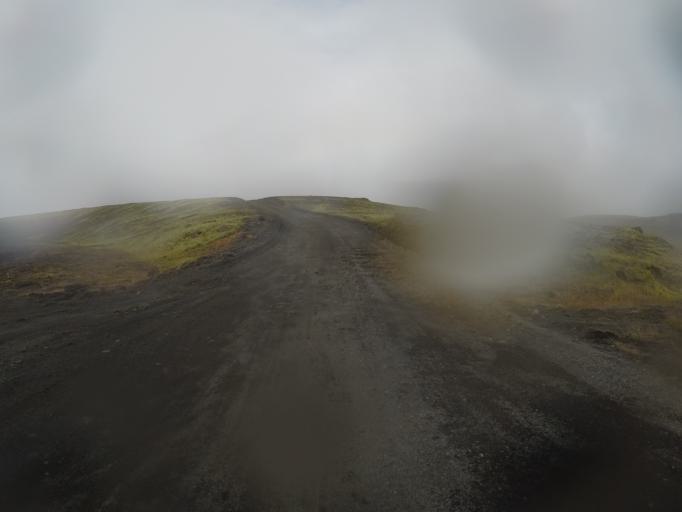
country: IS
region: South
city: Vestmannaeyjar
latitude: 63.9776
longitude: -18.8437
